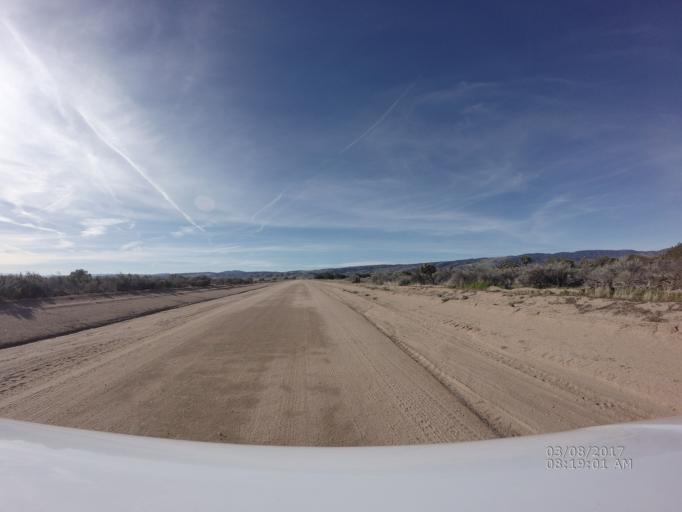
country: US
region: California
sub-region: Los Angeles County
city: Green Valley
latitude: 34.7635
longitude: -118.4490
